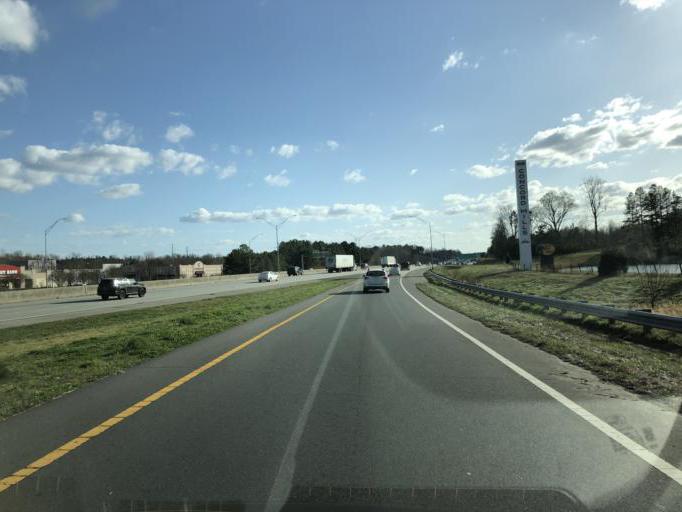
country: US
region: North Carolina
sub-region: Cabarrus County
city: Harrisburg
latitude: 35.3670
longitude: -80.7161
